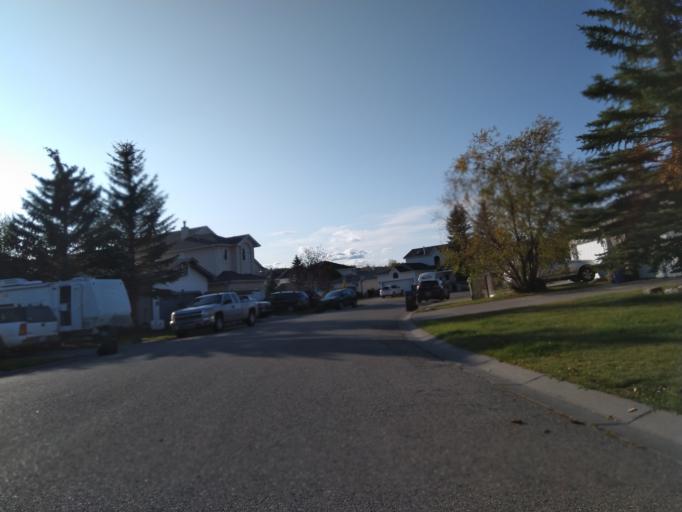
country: CA
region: Alberta
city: Cochrane
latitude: 51.1740
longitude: -114.4688
